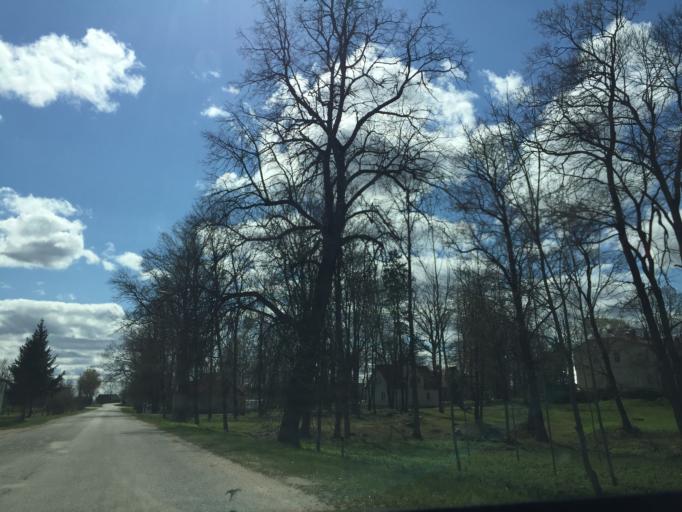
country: LV
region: Vilanu
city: Vilani
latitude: 56.7360
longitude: 27.0673
